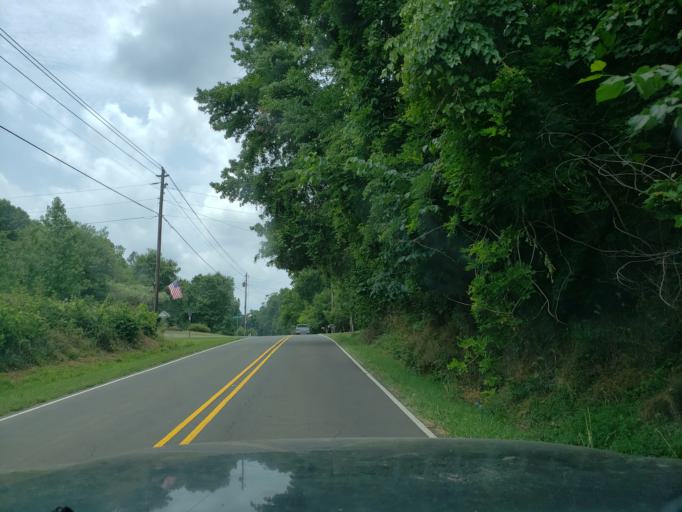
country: US
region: North Carolina
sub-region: Granville County
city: Butner
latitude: 36.1623
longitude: -78.8821
